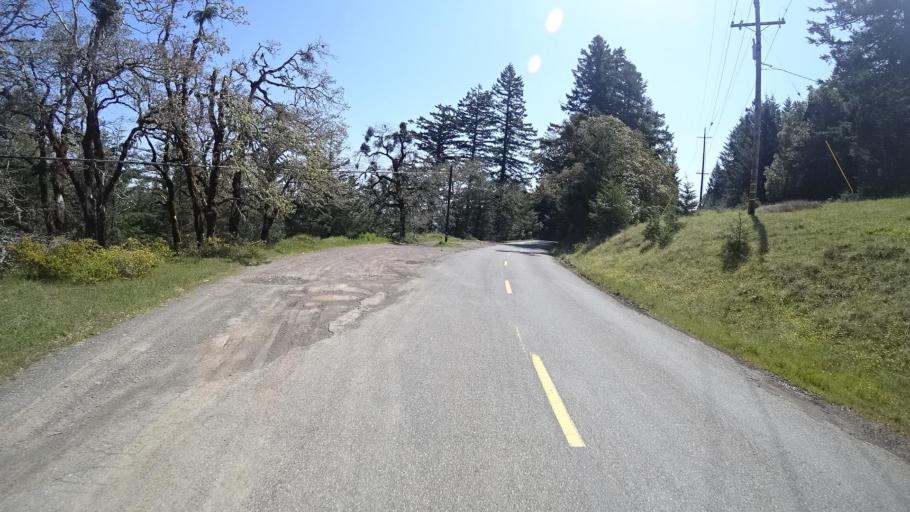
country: US
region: California
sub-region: Humboldt County
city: Redway
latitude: 40.0950
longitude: -123.6805
